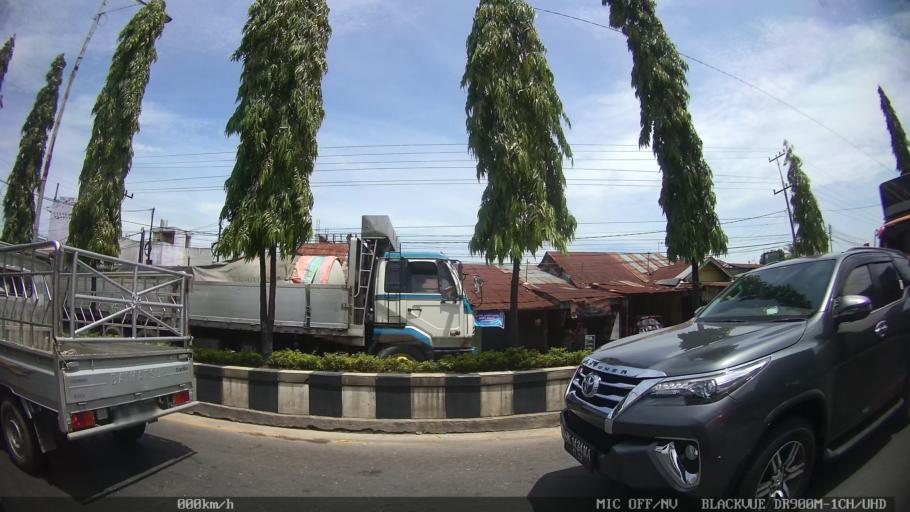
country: ID
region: North Sumatra
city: Percut
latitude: 3.5546
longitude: 98.8805
